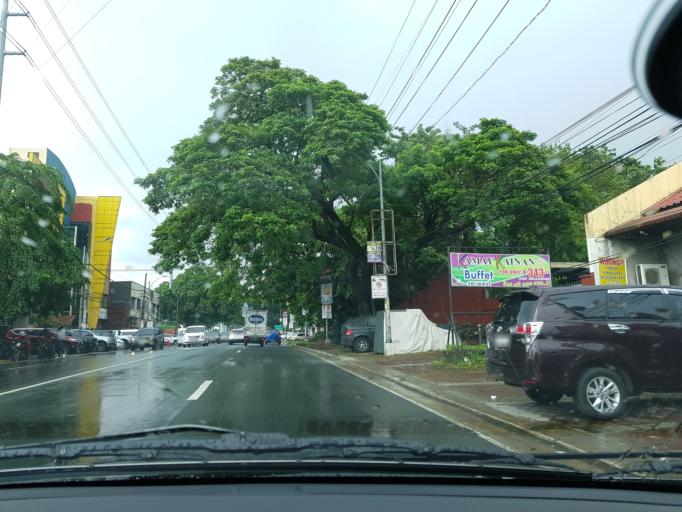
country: PH
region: Calabarzon
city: Del Monte
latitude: 14.6406
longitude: 121.0266
